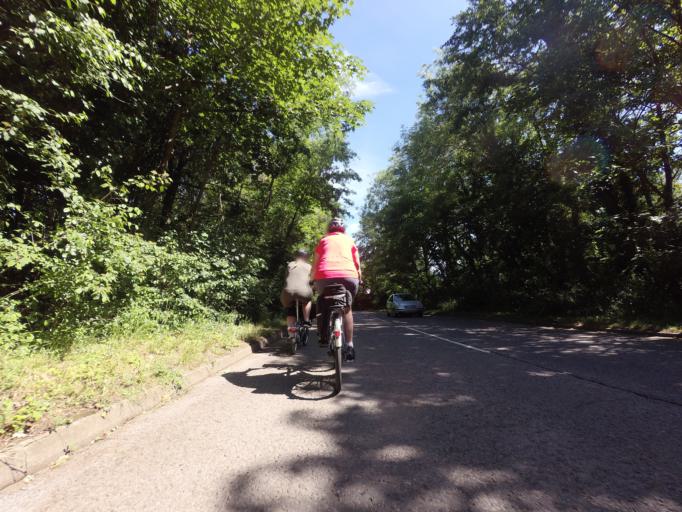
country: GB
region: England
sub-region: Medway
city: Rochester
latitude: 51.4080
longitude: 0.5254
